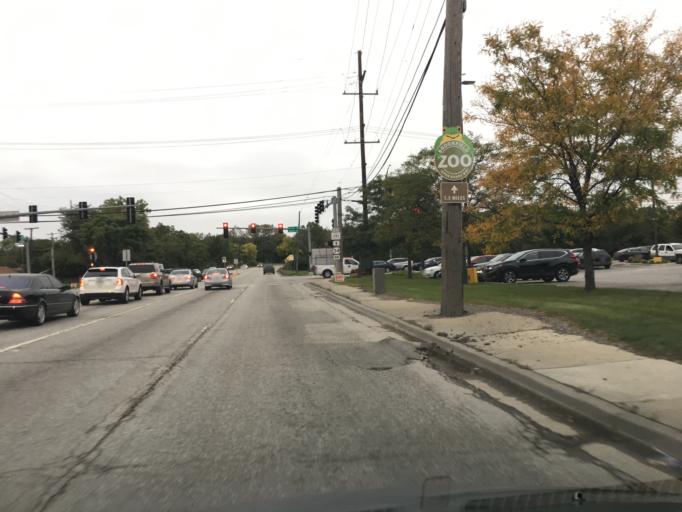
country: US
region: Illinois
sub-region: Cook County
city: Lyons
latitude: 41.8154
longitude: -87.8338
